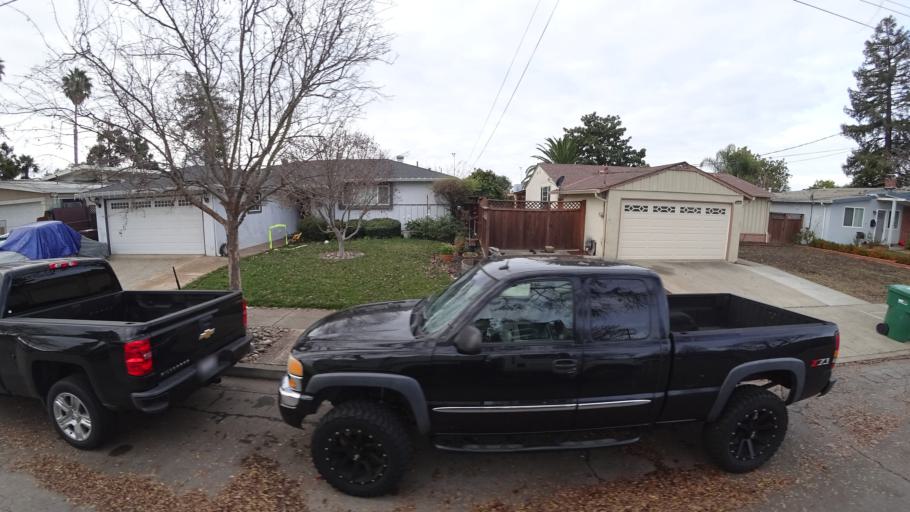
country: US
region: California
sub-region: Alameda County
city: Union City
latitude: 37.6166
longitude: -122.0421
